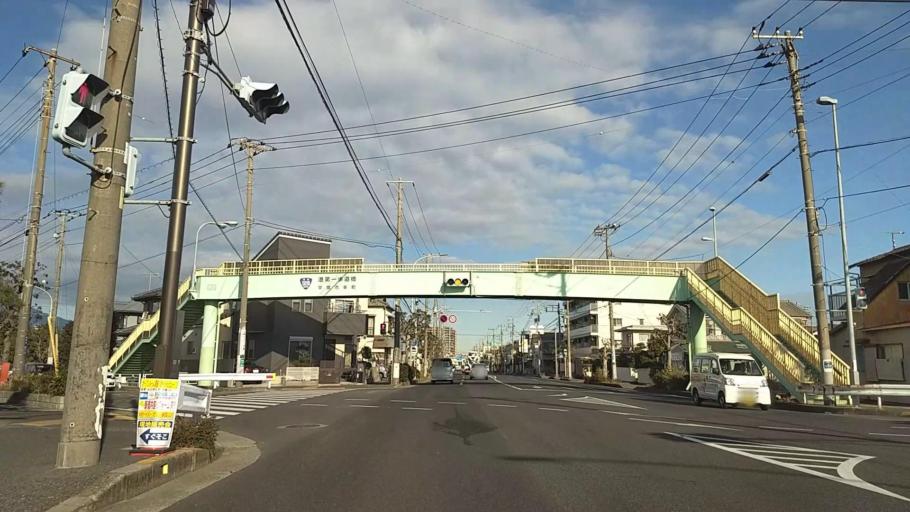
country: JP
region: Kanagawa
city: Hiratsuka
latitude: 35.3188
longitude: 139.3616
